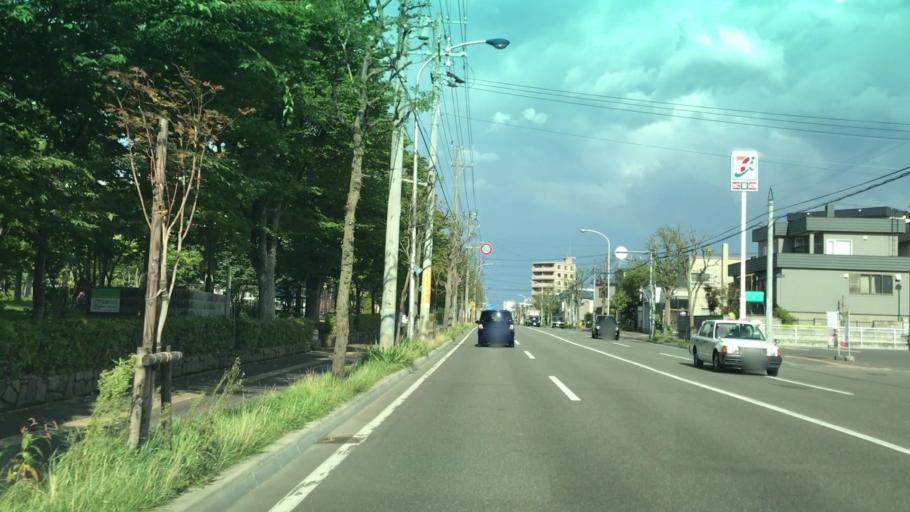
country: JP
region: Hokkaido
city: Sapporo
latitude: 43.0848
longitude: 141.2983
